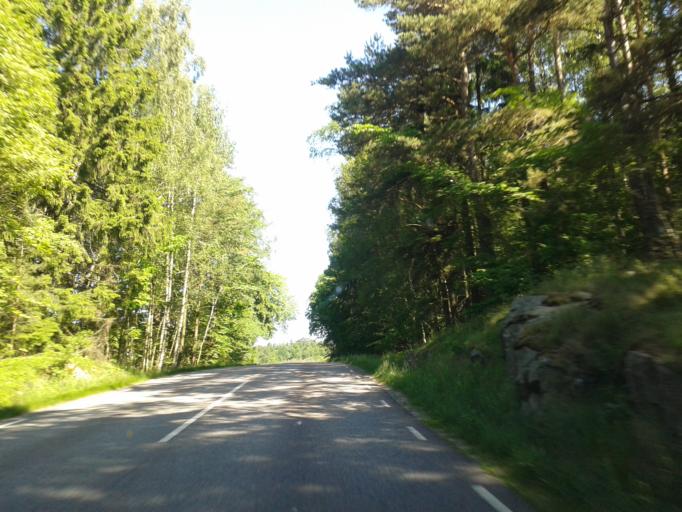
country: SE
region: Vaestra Goetaland
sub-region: Kungalvs Kommun
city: Kode
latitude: 57.9155
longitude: 11.9186
